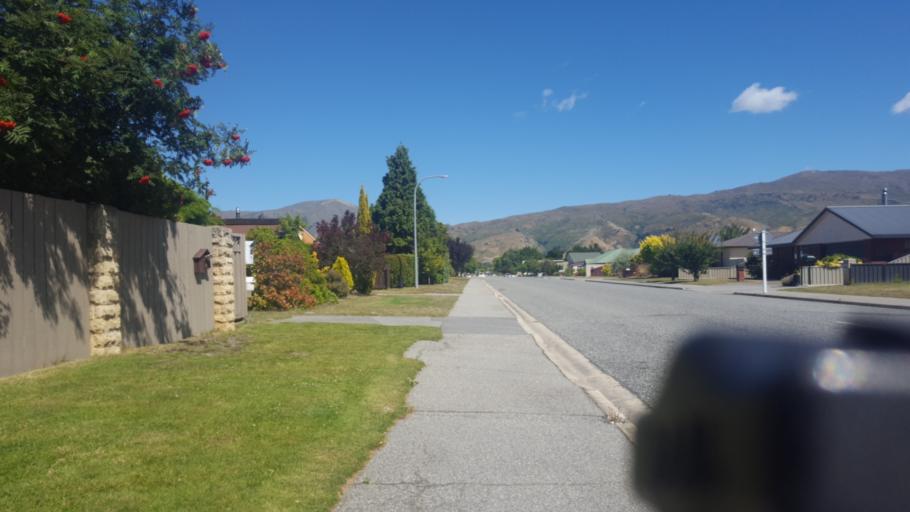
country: NZ
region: Otago
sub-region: Queenstown-Lakes District
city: Wanaka
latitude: -45.0451
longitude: 169.2023
